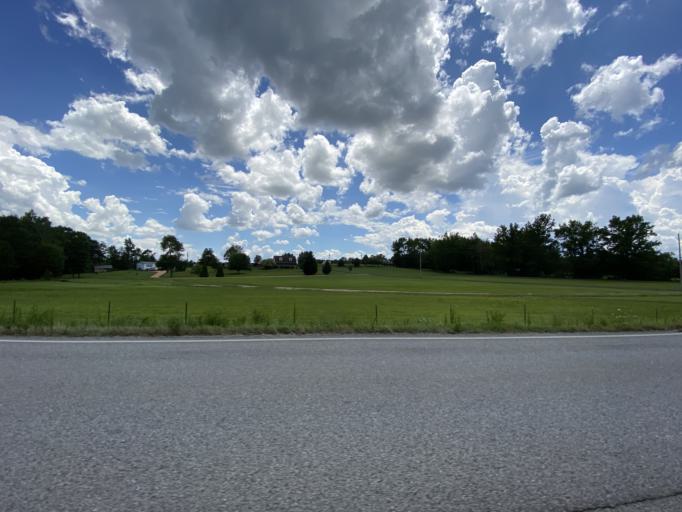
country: US
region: Alabama
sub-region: Lauderdale County
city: Underwood-Petersville
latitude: 34.9465
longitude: -87.8646
